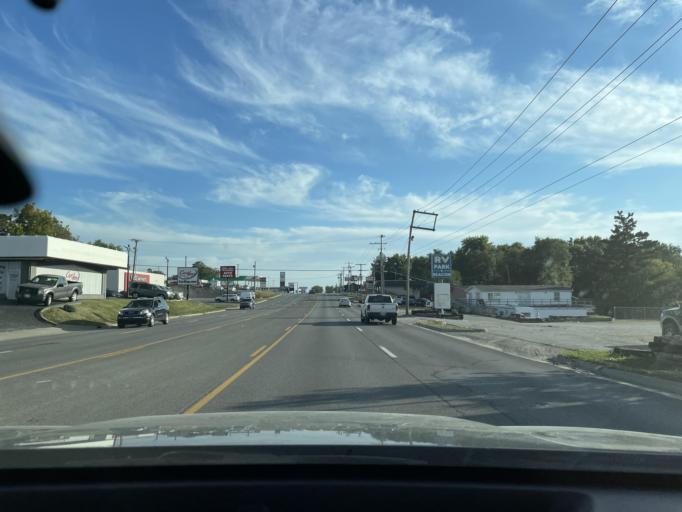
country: US
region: Missouri
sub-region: Buchanan County
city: Saint Joseph
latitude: 39.7593
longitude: -94.8038
